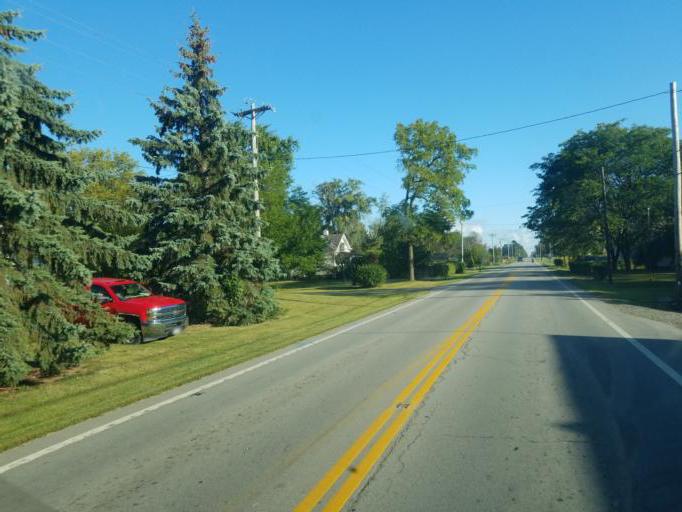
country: US
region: Ohio
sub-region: Lorain County
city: Camden
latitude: 41.1716
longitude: -82.3090
